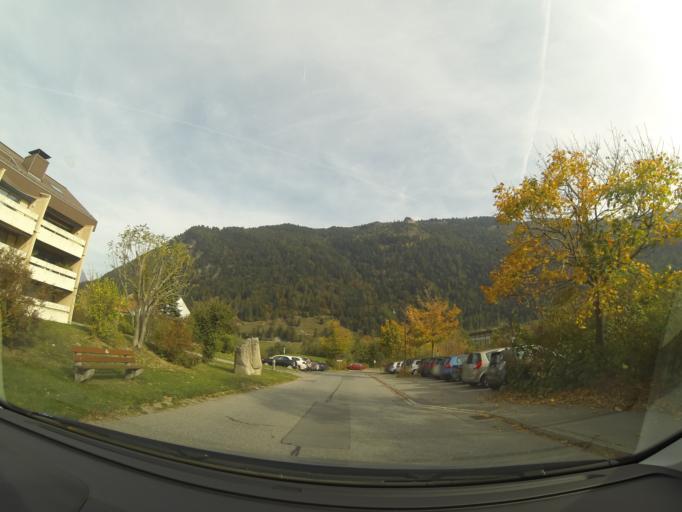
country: CH
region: Saint Gallen
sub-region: Wahlkreis Sarganserland
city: Bad Ragaz
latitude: 46.9704
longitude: 9.4823
